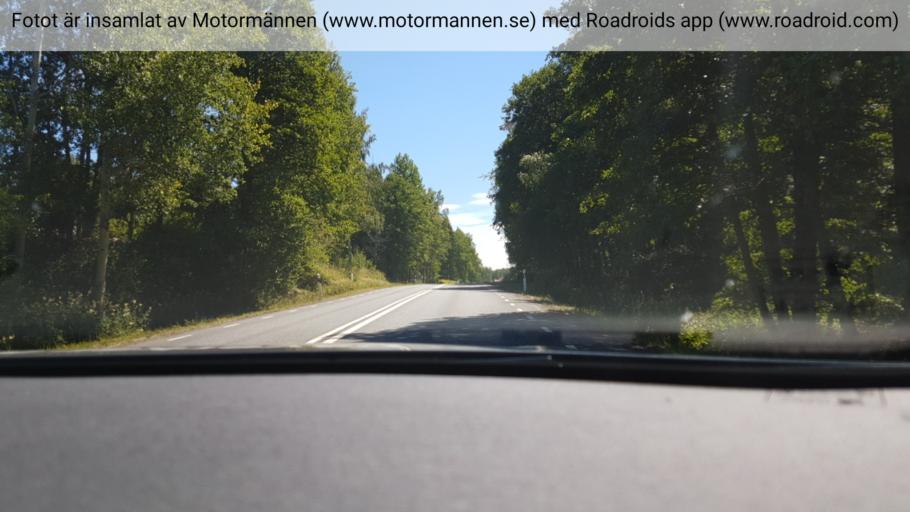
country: SE
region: Joenkoeping
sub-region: Jonkopings Kommun
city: Graenna
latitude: 58.0112
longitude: 14.5295
